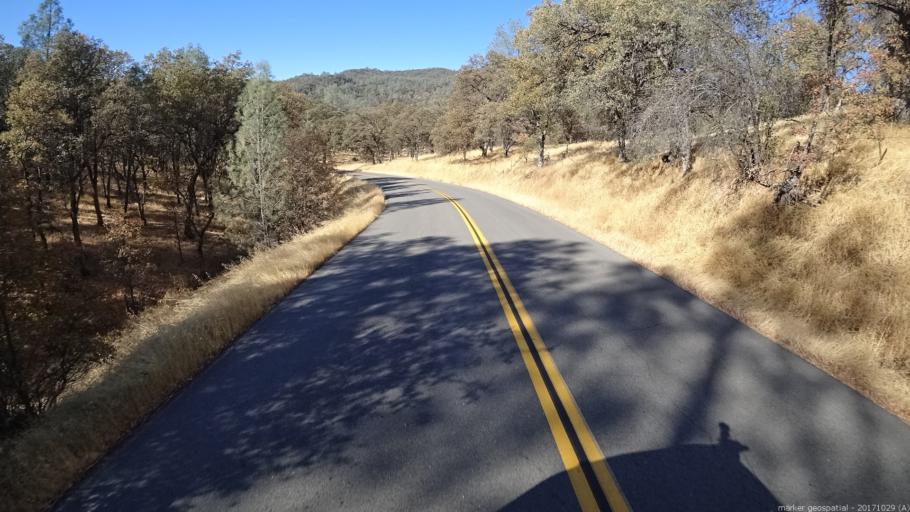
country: US
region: California
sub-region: Shasta County
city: Shasta
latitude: 40.4404
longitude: -122.7049
